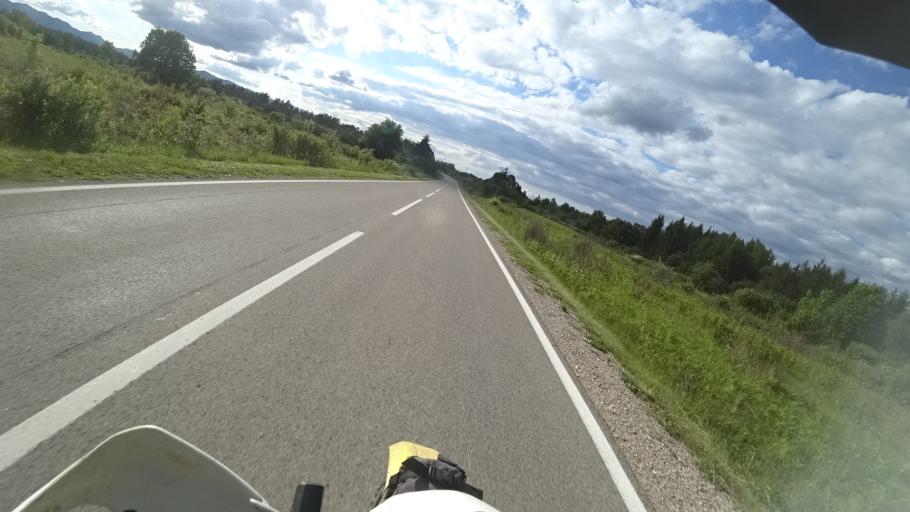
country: HR
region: Licko-Senjska
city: Gospic
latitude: 44.5038
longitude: 15.4472
